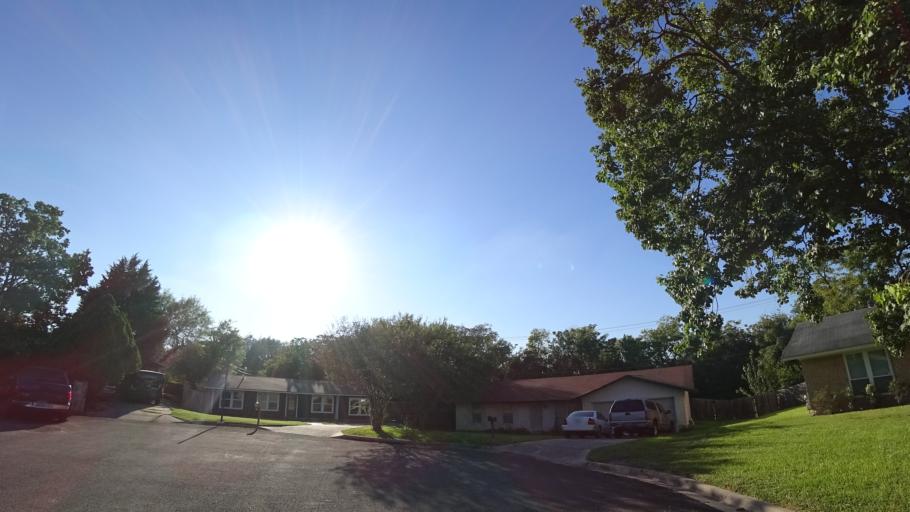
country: US
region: Texas
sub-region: Travis County
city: Austin
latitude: 30.2179
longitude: -97.7394
